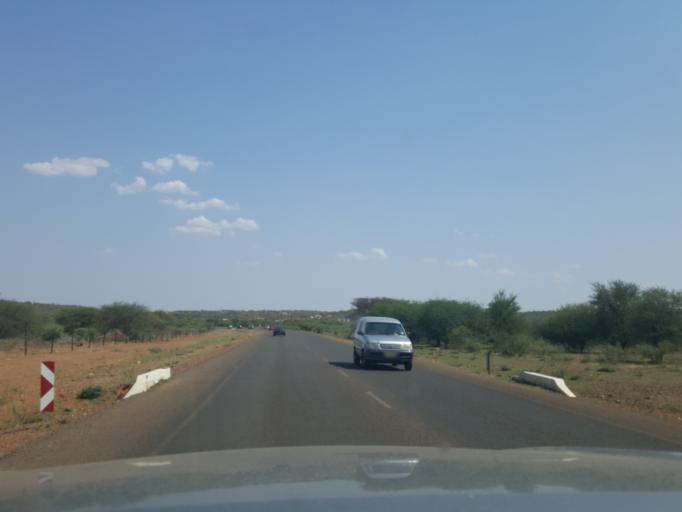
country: BW
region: South East
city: Ramotswa
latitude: -24.8566
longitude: 25.8298
